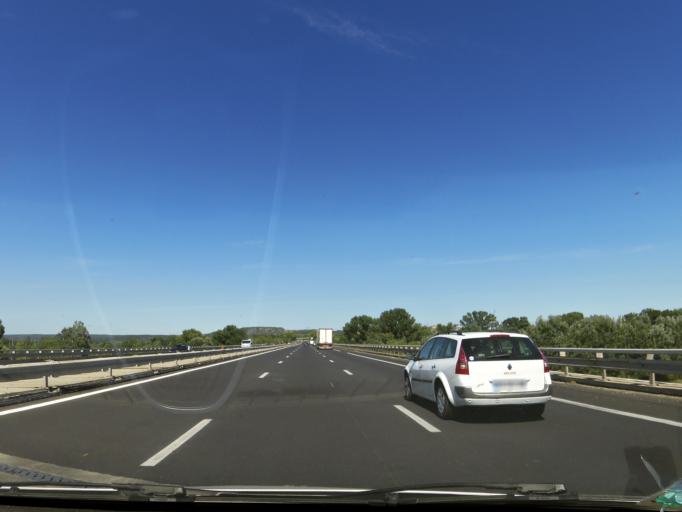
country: FR
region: Languedoc-Roussillon
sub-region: Departement du Gard
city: Remoulins
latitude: 43.9195
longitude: 4.5794
